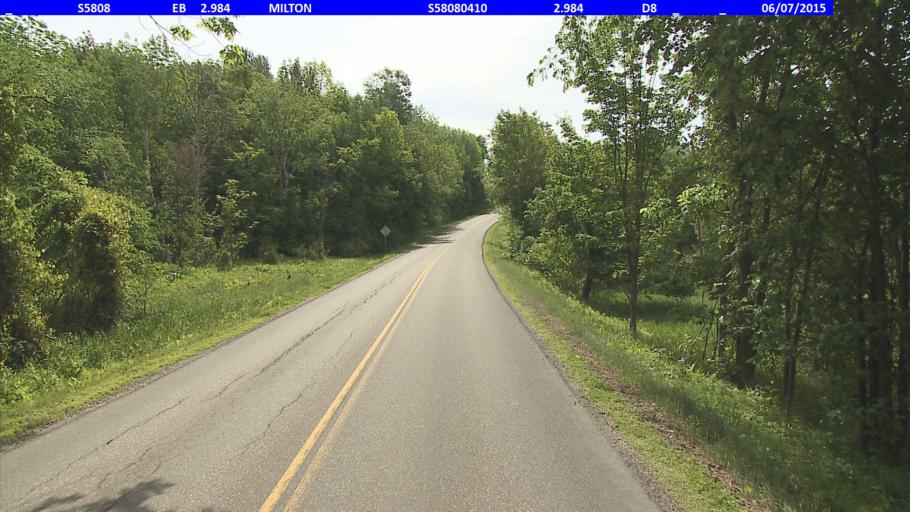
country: US
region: Vermont
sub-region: Chittenden County
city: Milton
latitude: 44.6427
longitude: -73.0594
